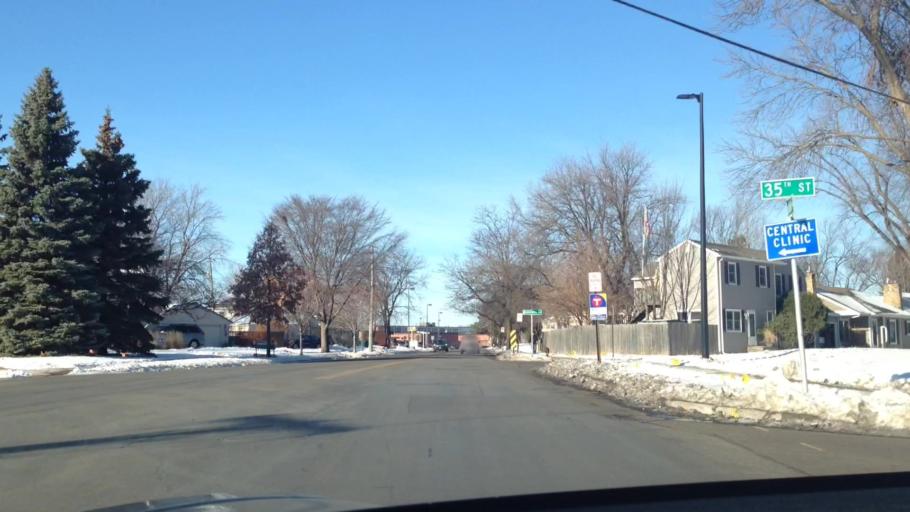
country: US
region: Minnesota
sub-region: Hennepin County
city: Saint Louis Park
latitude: 44.9399
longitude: -93.3575
